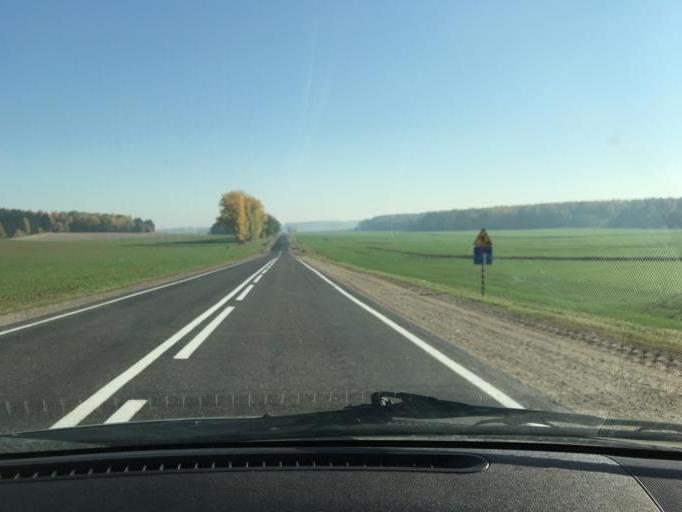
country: BY
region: Minsk
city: Klyetsk
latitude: 52.9671
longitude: 26.5701
